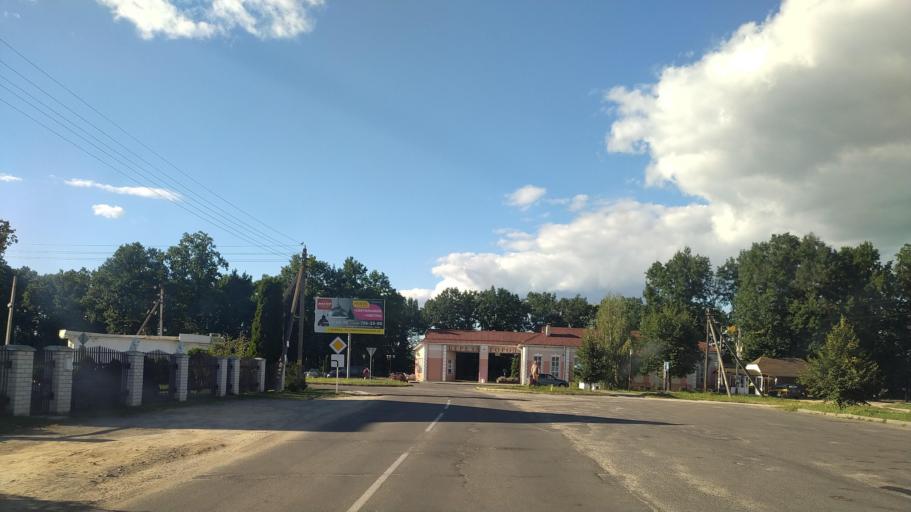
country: BY
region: Brest
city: Byaroza
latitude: 52.5467
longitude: 24.9741
